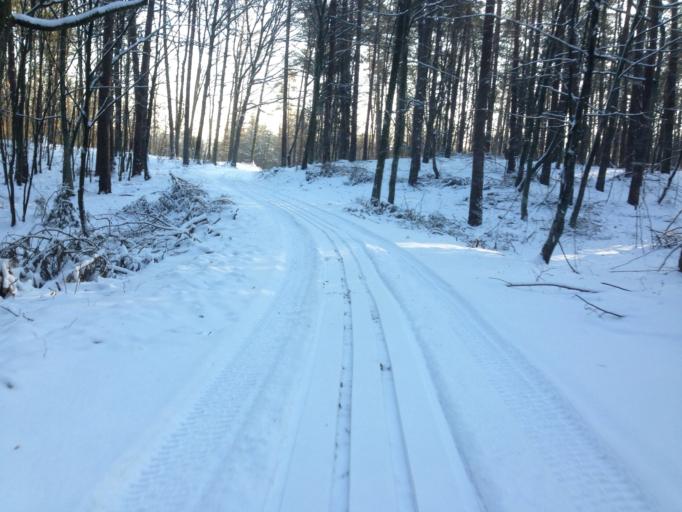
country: PL
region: Kujawsko-Pomorskie
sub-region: Powiat brodnicki
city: Gorzno
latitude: 53.1886
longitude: 19.6806
